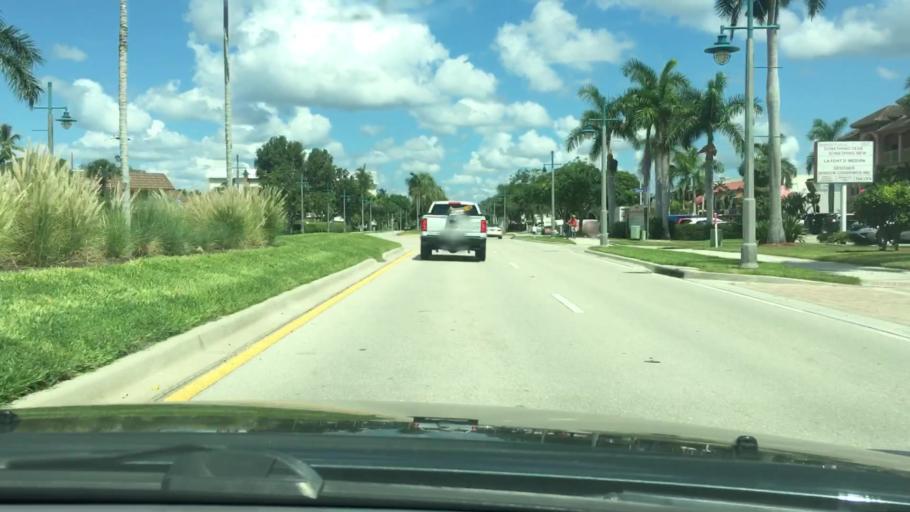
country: US
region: Florida
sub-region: Collier County
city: Marco
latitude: 25.9416
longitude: -81.7326
